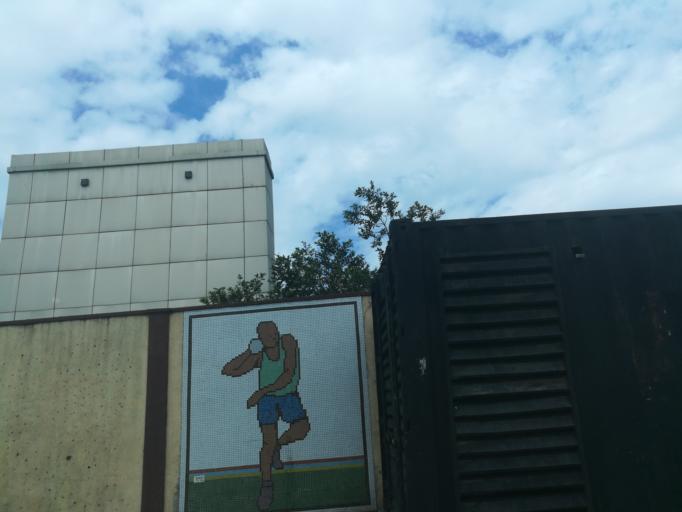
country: NG
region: Lagos
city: Agege
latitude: 6.6237
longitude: 3.3290
